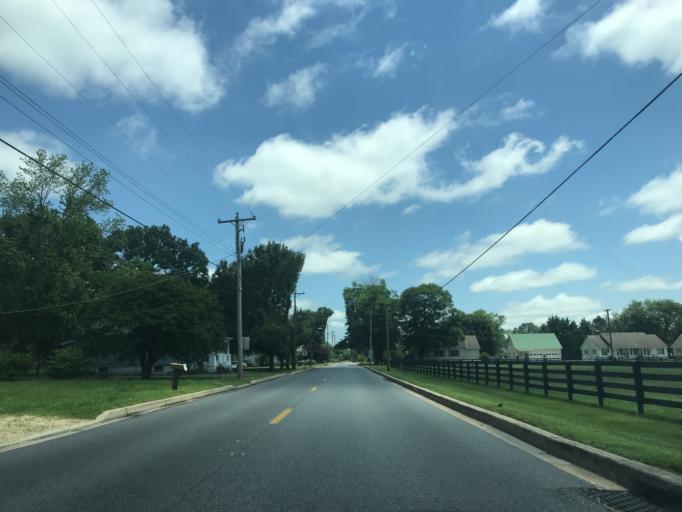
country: US
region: Maryland
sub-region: Caroline County
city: Federalsburg
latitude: 38.6904
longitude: -75.7836
